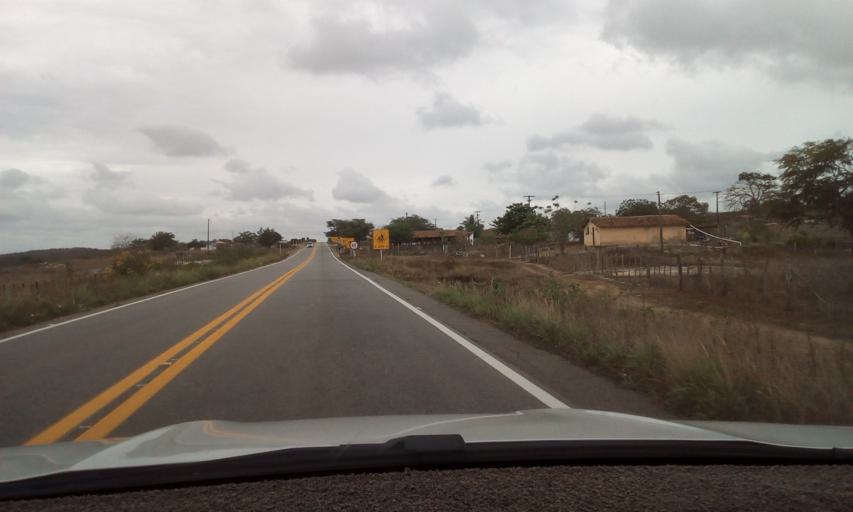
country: BR
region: Paraiba
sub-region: Areia
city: Remigio
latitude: -6.9218
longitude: -35.8461
